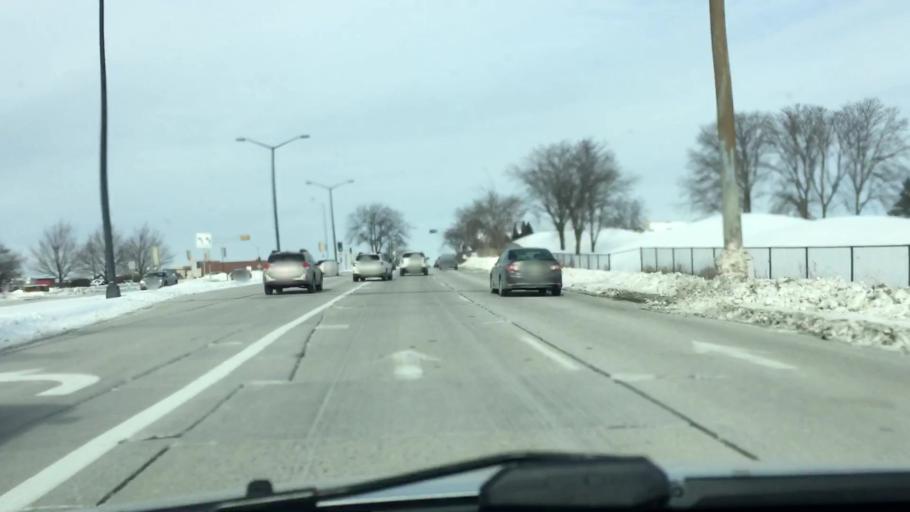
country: US
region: Wisconsin
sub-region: Waukesha County
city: Elm Grove
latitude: 43.0274
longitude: -88.1068
